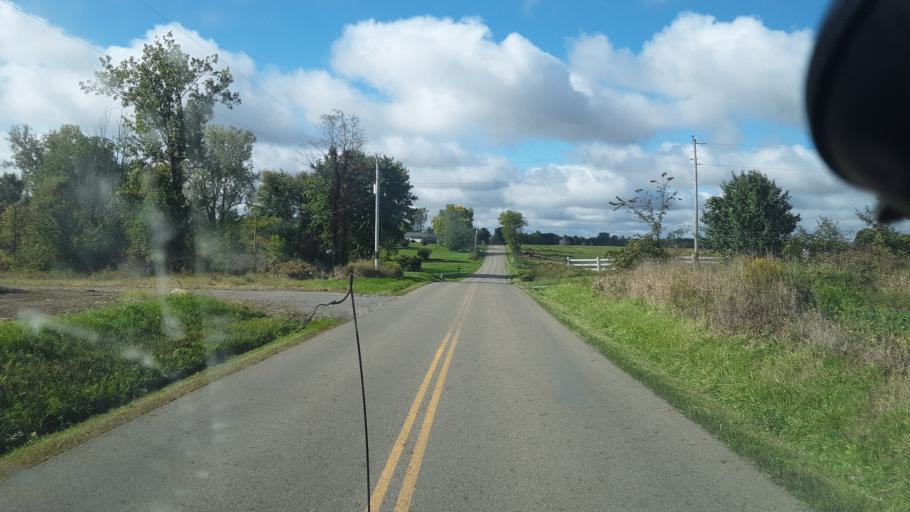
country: US
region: Ohio
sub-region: Knox County
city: Centerburg
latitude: 40.2863
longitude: -82.6364
